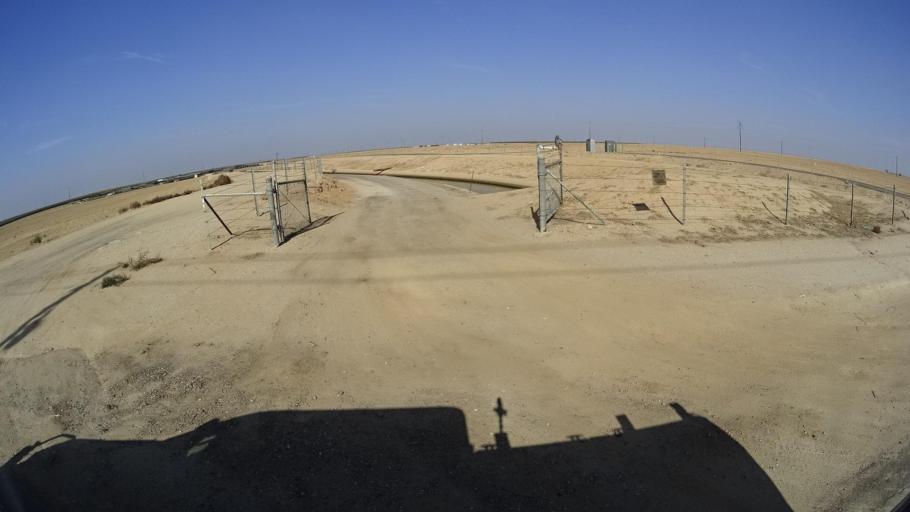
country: US
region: California
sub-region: Kern County
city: Oildale
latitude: 35.5299
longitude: -119.1106
